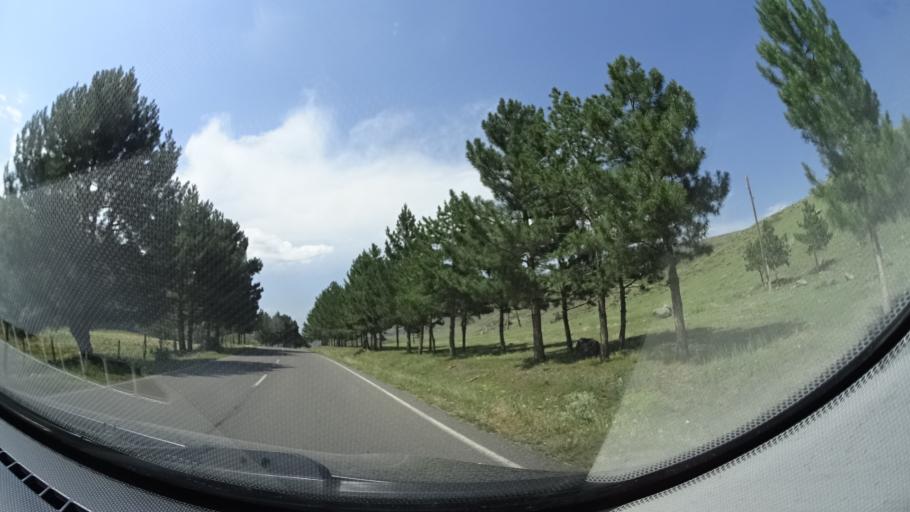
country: GE
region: Samtskhe-Javakheti
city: Aspindza
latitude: 41.4251
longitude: 43.3206
